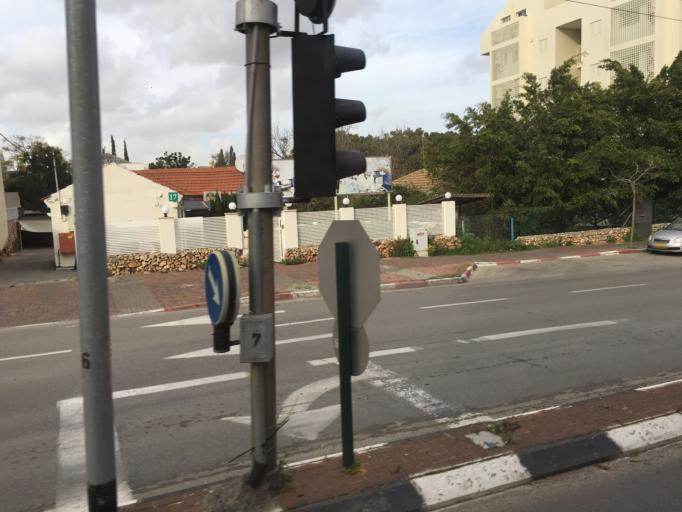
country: IL
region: Central District
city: Kfar Saba
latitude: 32.1778
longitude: 34.8977
